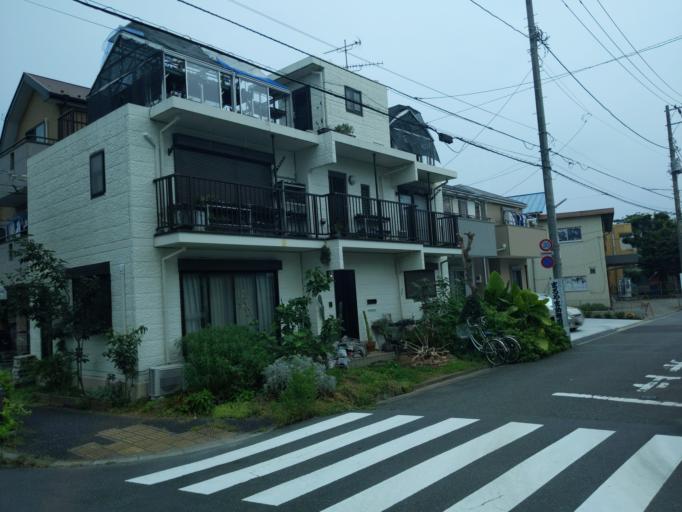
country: JP
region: Saitama
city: Wako
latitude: 35.7818
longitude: 139.6524
